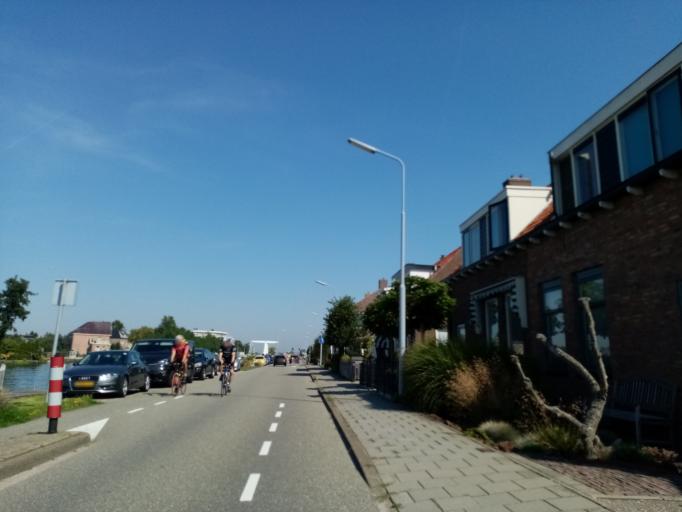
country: NL
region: South Holland
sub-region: Gemeente Lisse
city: Lisse
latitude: 52.2527
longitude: 4.5689
